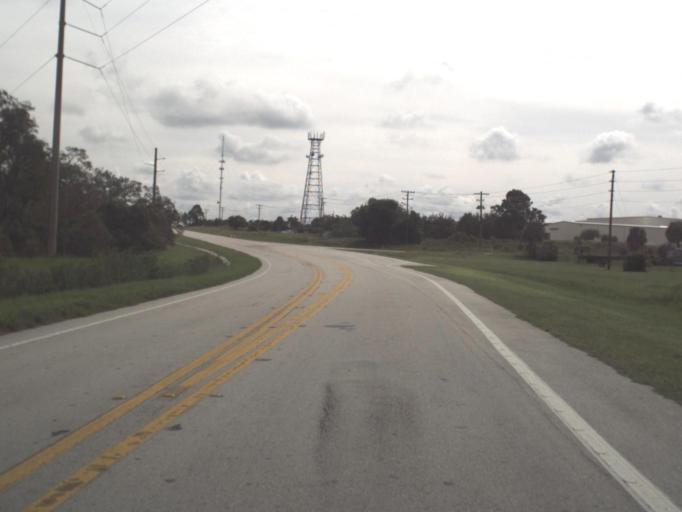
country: US
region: Florida
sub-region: Highlands County
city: Placid Lakes
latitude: 27.2088
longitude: -81.3402
